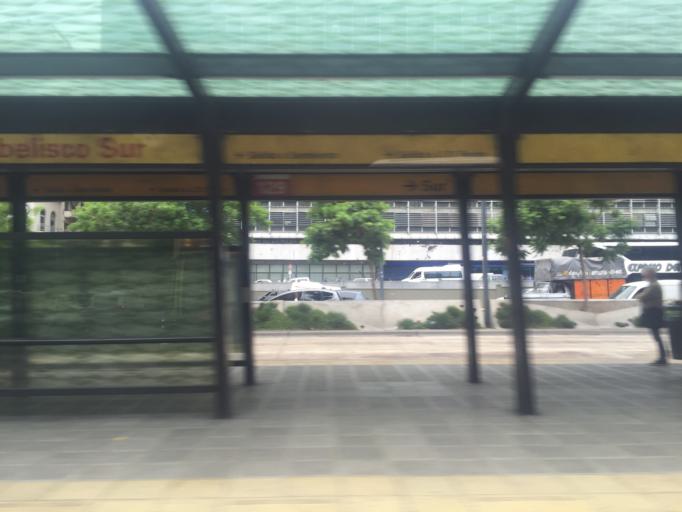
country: AR
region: Buenos Aires F.D.
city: Buenos Aires
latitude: -34.6053
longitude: -58.3815
